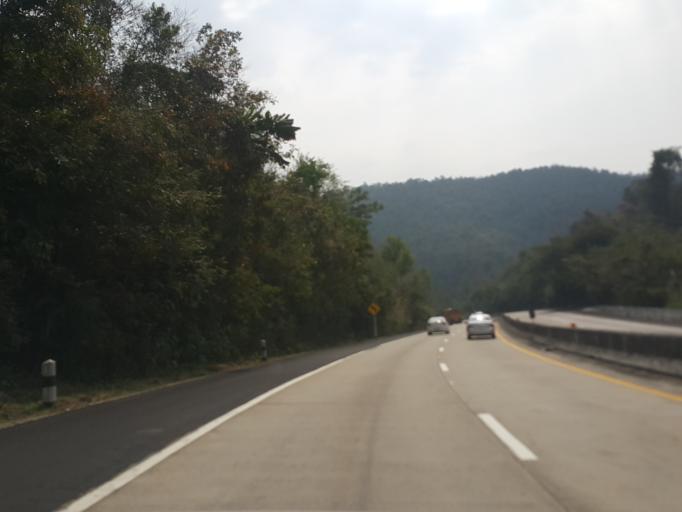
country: TH
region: Lampang
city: Hang Chat
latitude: 18.3312
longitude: 99.2534
